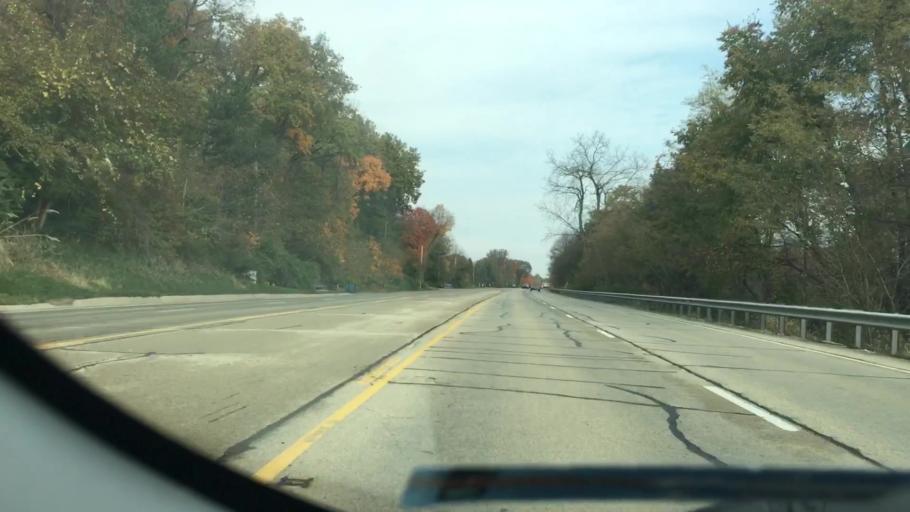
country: US
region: Illinois
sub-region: Peoria County
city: Peoria Heights
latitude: 40.7808
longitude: -89.5772
